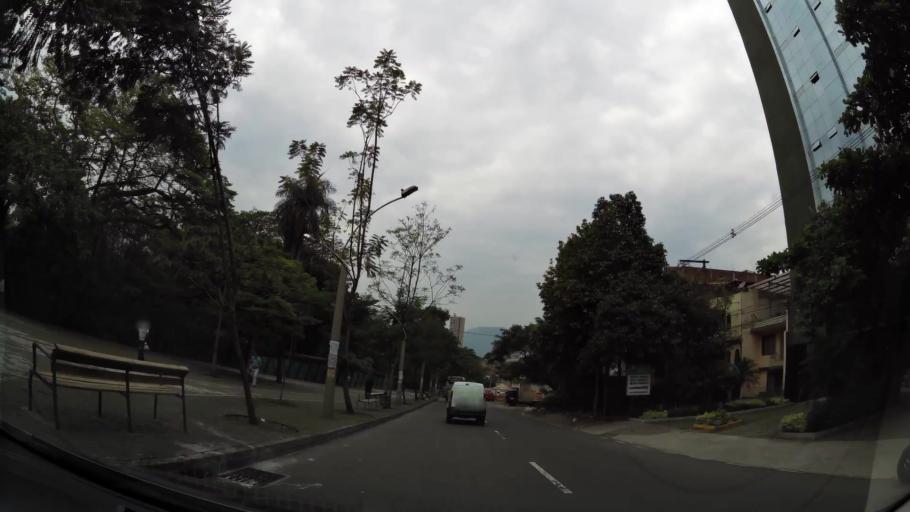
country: CO
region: Antioquia
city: Medellin
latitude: 6.2689
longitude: -75.5620
